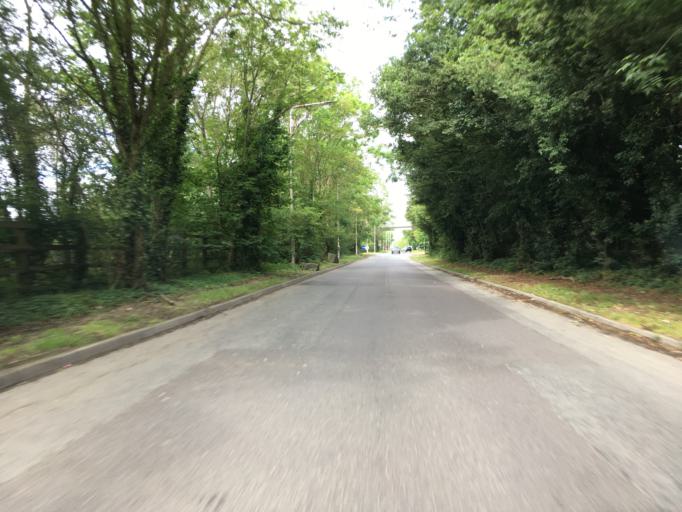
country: GB
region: England
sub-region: Wiltshire
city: Norton
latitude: 51.5108
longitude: -2.1573
